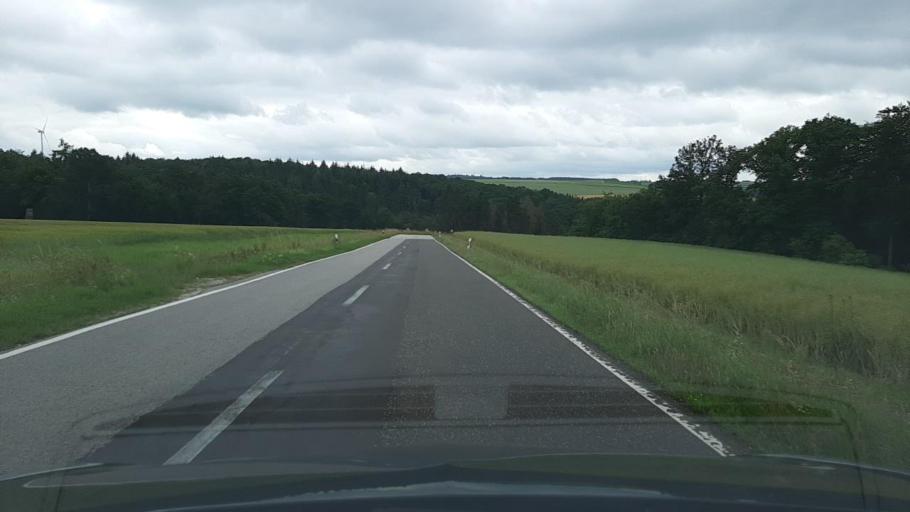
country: DE
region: Rheinland-Pfalz
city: Beltheim
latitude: 50.0983
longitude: 7.4570
